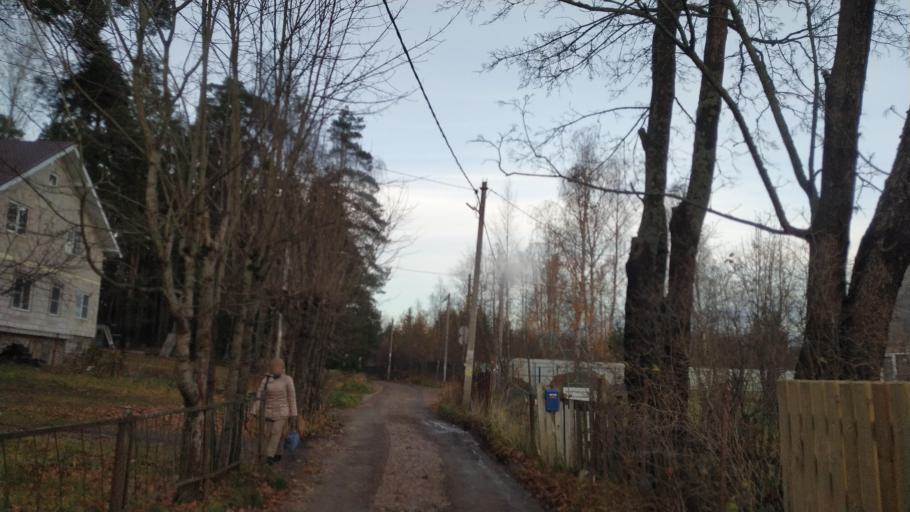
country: RU
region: Leningrad
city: Sosnovyy Bor
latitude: 59.9553
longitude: 29.0992
